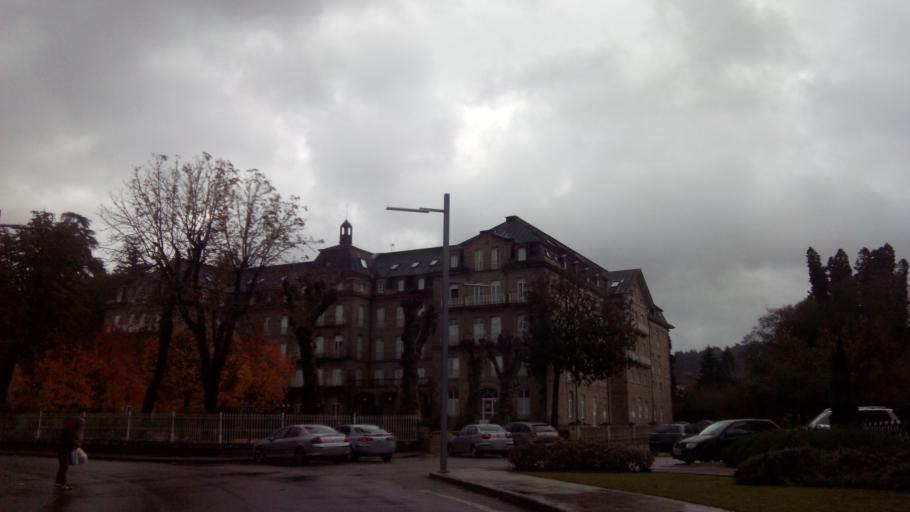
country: ES
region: Galicia
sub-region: Provincia de Pontevedra
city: Mondariz-Balneario
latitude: 42.2269
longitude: -8.4673
